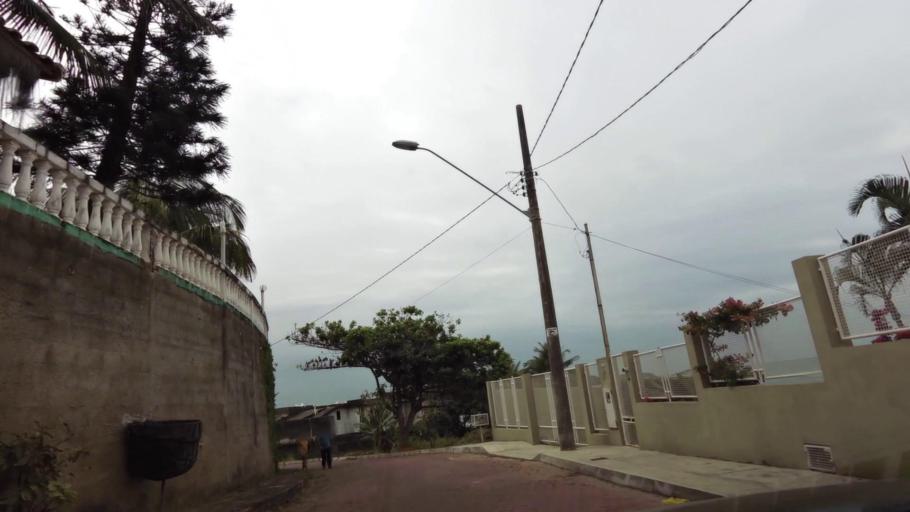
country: BR
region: Espirito Santo
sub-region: Guarapari
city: Guarapari
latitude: -20.6658
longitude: -40.4936
